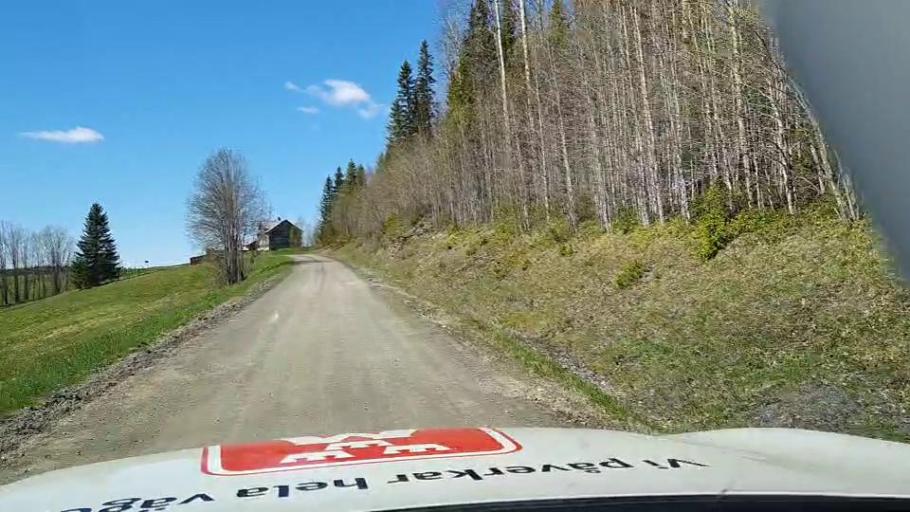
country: SE
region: Jaemtland
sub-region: Krokoms Kommun
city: Valla
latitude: 63.6592
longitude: 13.6201
